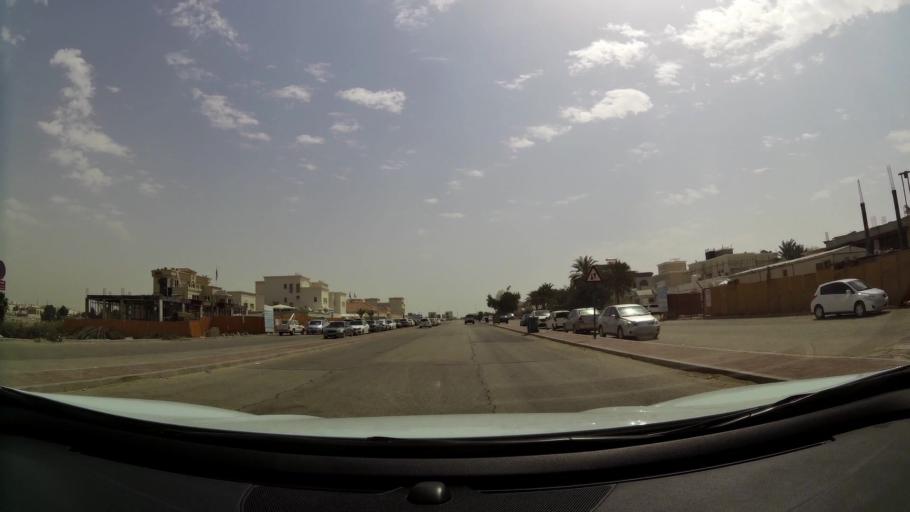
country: AE
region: Abu Dhabi
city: Abu Dhabi
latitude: 24.3011
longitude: 54.6284
